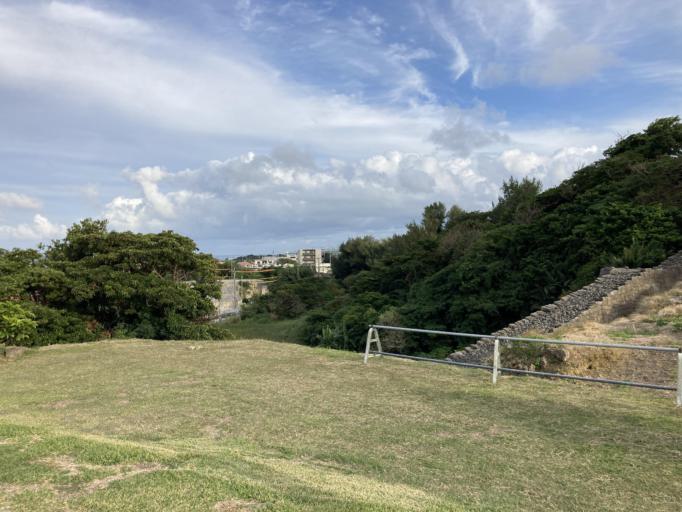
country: JP
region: Okinawa
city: Katsuren-haebaru
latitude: 26.3305
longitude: 127.8797
